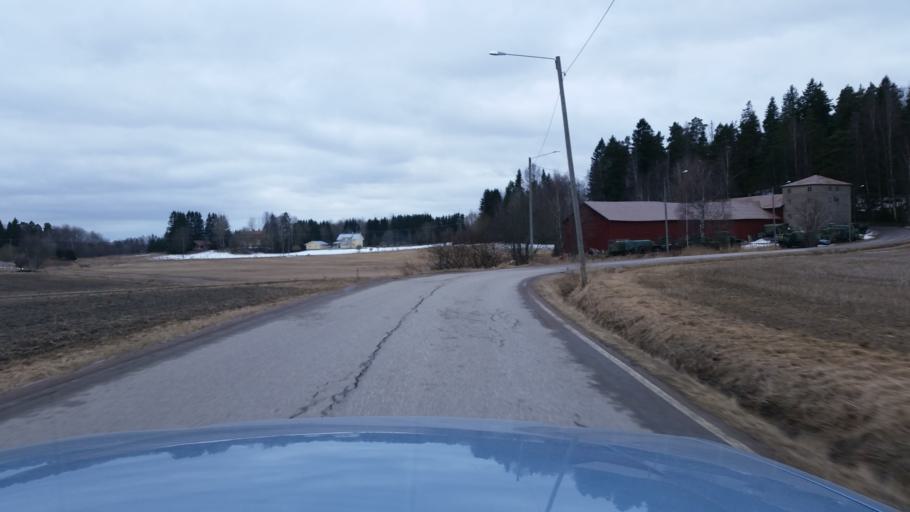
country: FI
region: Uusimaa
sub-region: Helsinki
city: Espoo
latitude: 60.2797
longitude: 24.6727
